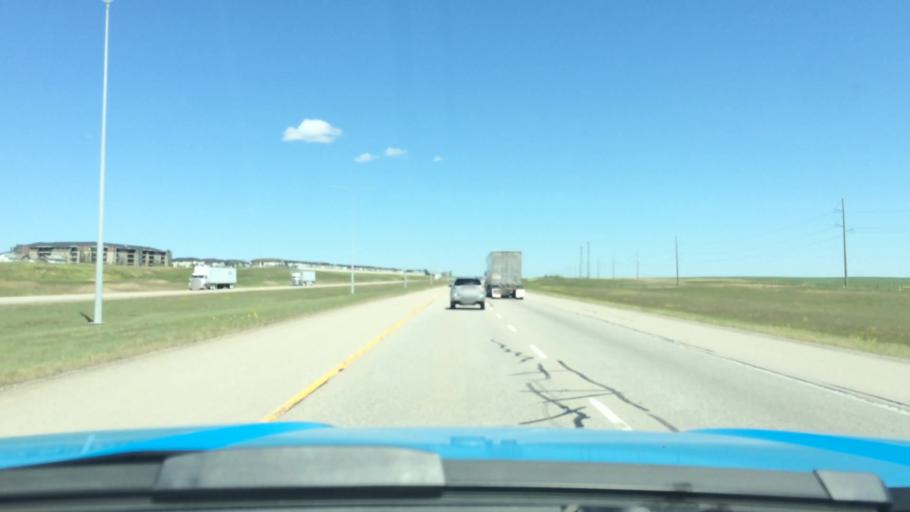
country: CA
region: Alberta
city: Chestermere
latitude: 51.1138
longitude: -113.9206
